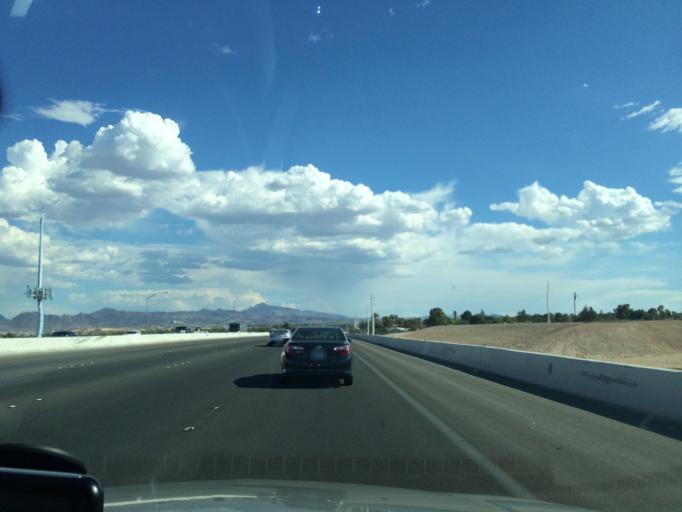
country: US
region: Nevada
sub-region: Clark County
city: Winchester
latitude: 36.1152
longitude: -115.0829
